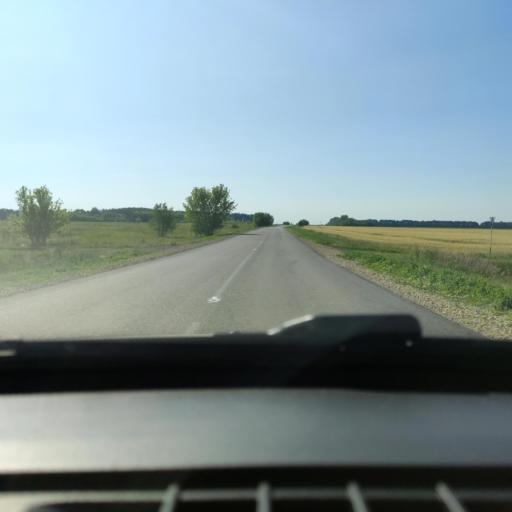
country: RU
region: Voronezj
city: Sadovoye
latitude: 51.6450
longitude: 40.3786
